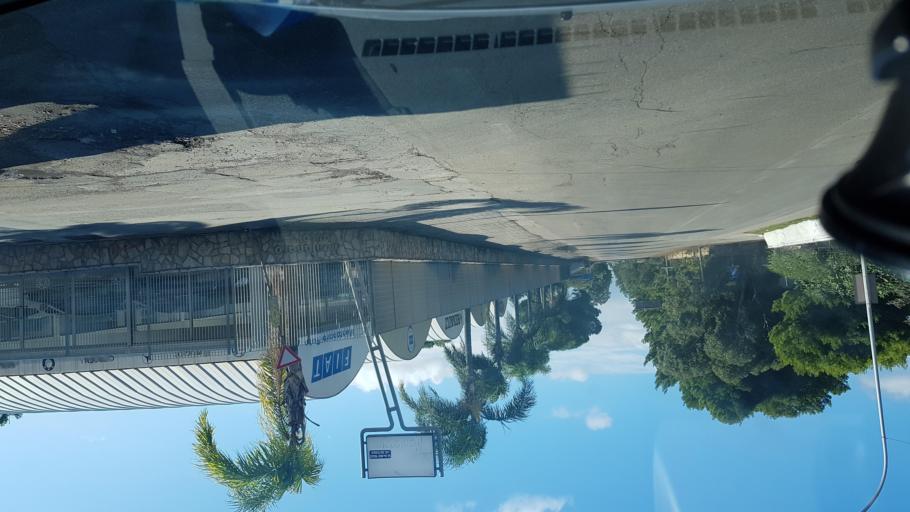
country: IT
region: Apulia
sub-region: Provincia di Brindisi
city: San Vito dei Normanni
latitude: 40.6575
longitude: 17.7199
